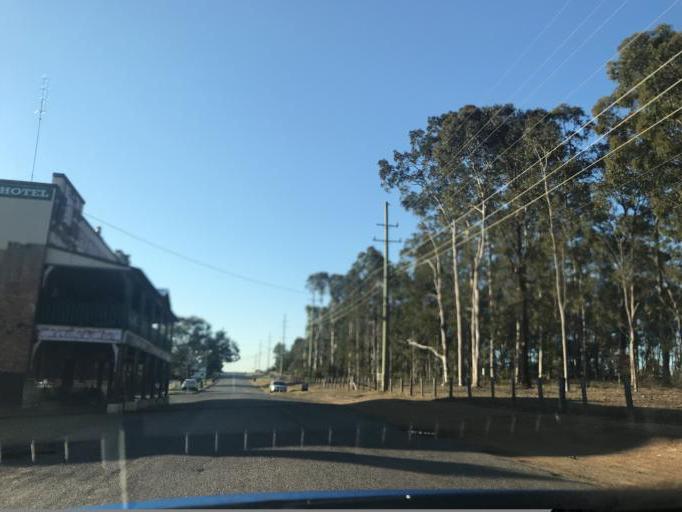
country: AU
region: New South Wales
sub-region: Cessnock
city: Cessnock
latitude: -32.9043
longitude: 151.2824
